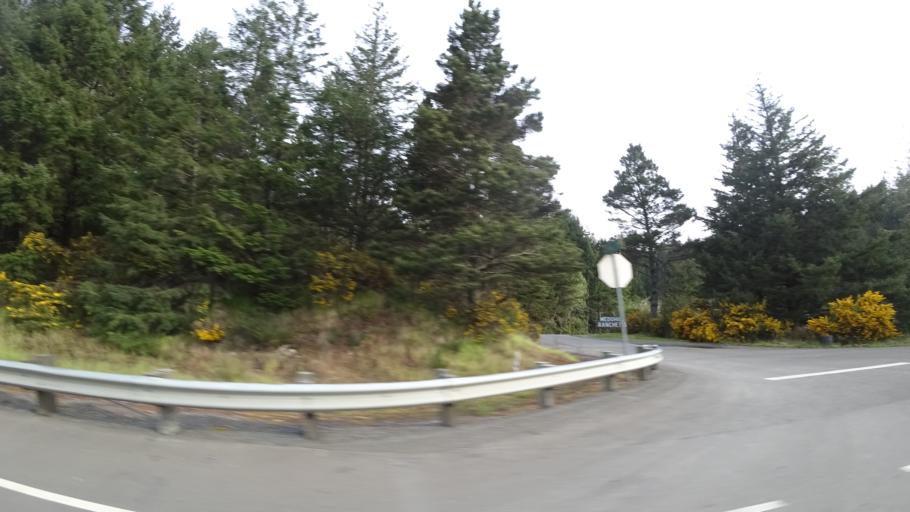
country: US
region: Oregon
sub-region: Coos County
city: Bandon
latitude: 43.1929
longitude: -124.3470
